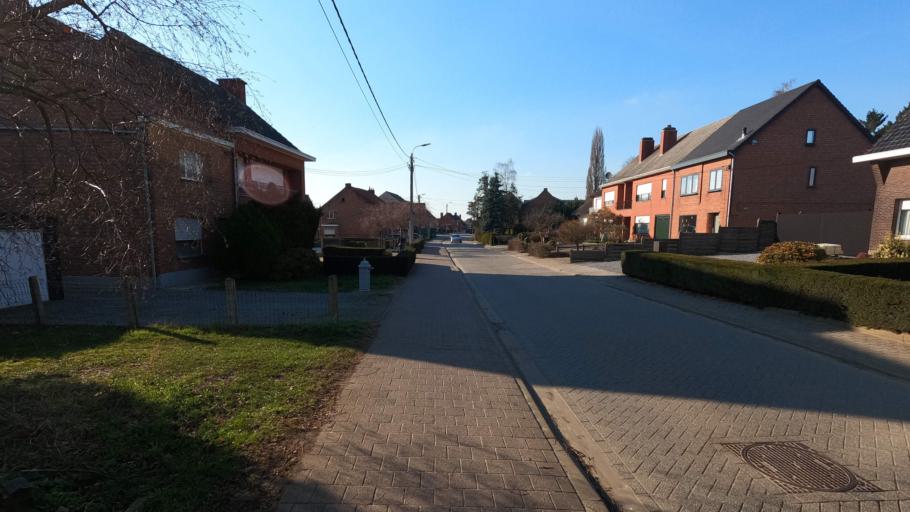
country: BE
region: Flanders
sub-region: Provincie Antwerpen
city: Heist-op-den-Berg
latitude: 51.0781
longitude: 4.7103
